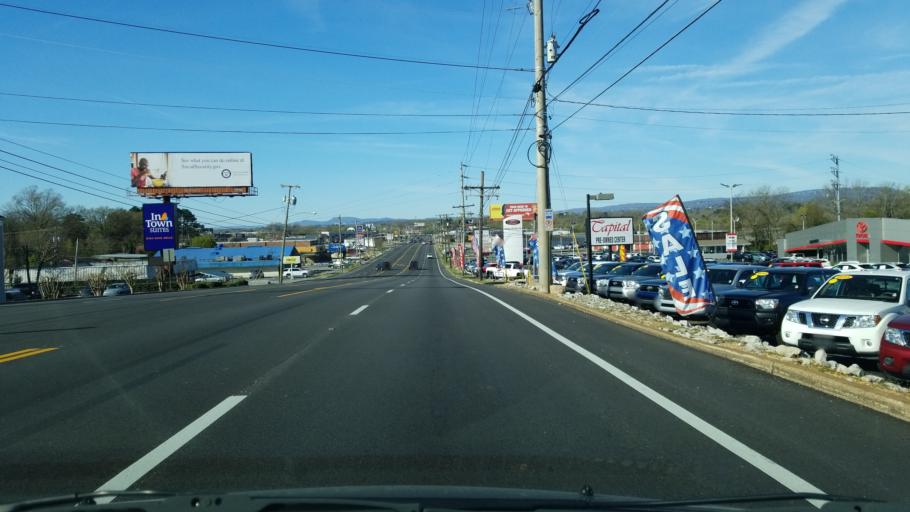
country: US
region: Tennessee
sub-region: Hamilton County
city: East Ridge
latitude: 35.0200
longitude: -85.2024
